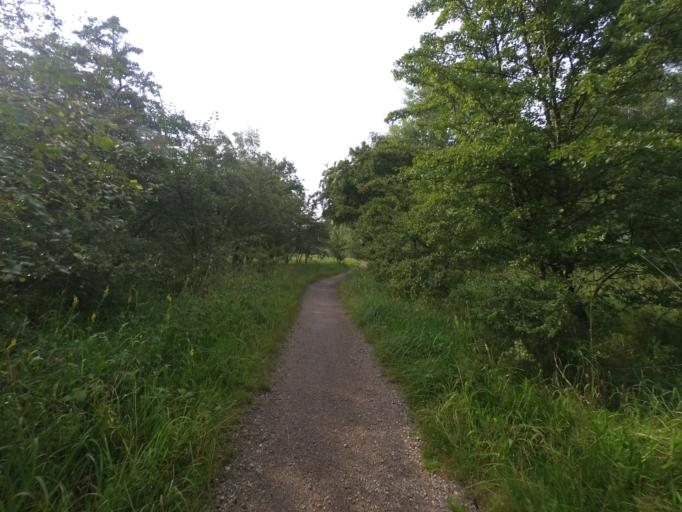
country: DE
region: Schleswig-Holstein
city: Glinde
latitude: 53.5003
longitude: 10.1816
